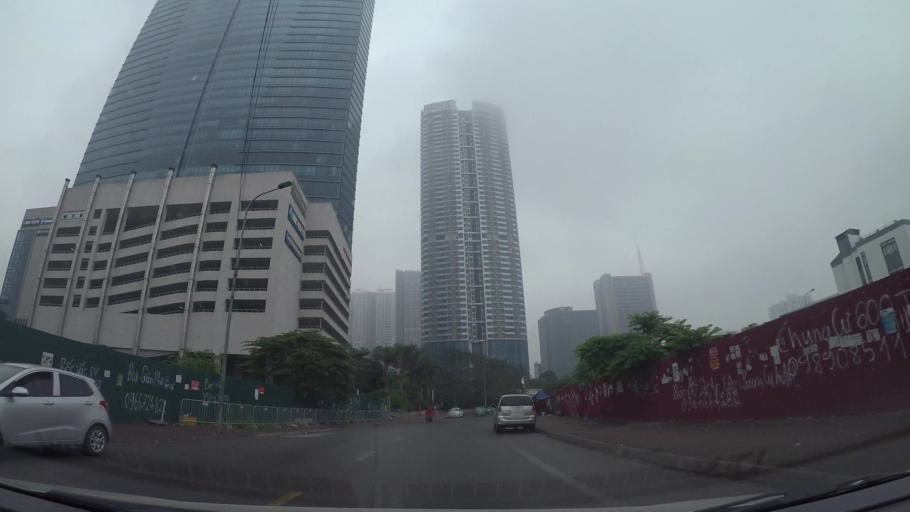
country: VN
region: Ha Noi
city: Cau Giay
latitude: 21.0164
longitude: 105.7854
